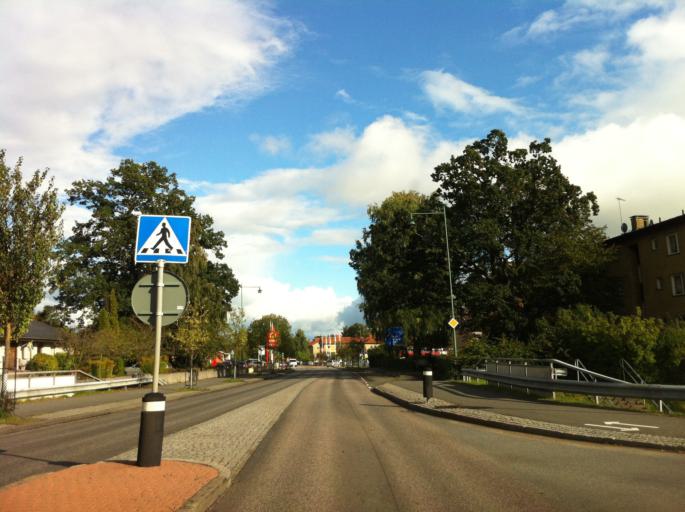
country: SE
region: Skane
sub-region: Hassleholms Kommun
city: Tormestorp
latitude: 56.1618
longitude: 13.6013
